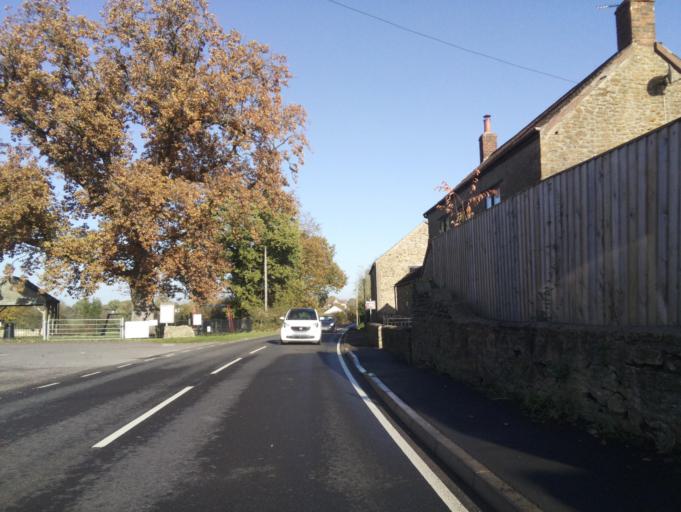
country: GB
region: England
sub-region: Somerset
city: Bruton
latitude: 51.1740
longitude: -2.4141
